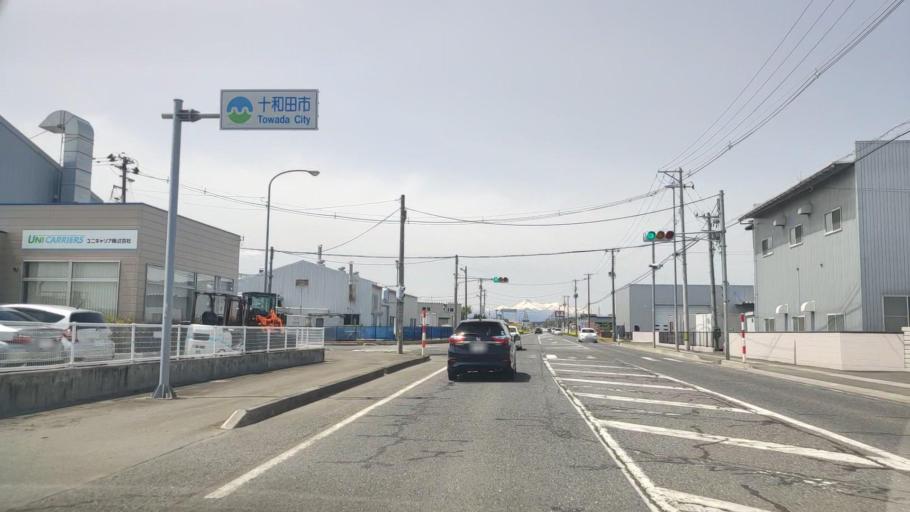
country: JP
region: Aomori
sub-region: Misawa Shi
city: Inuotose
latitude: 40.6106
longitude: 141.2744
